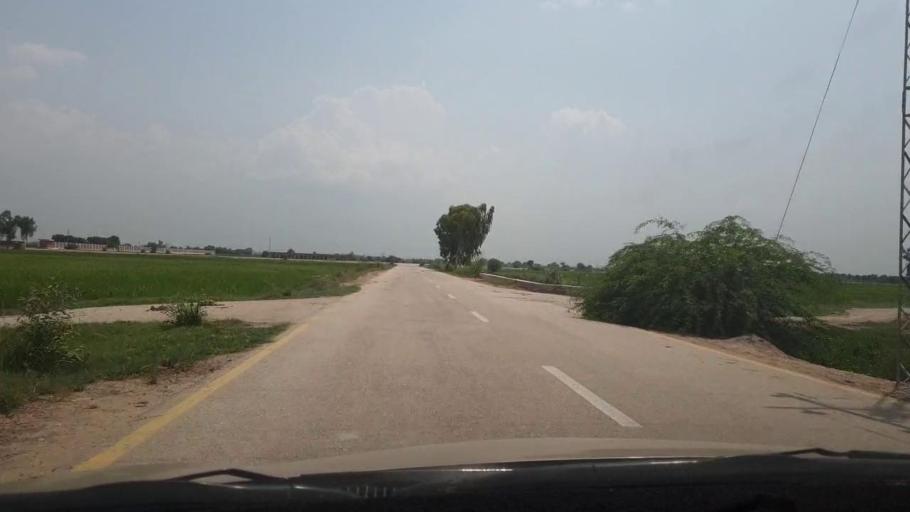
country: PK
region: Sindh
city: Naudero
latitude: 27.6974
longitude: 68.3337
